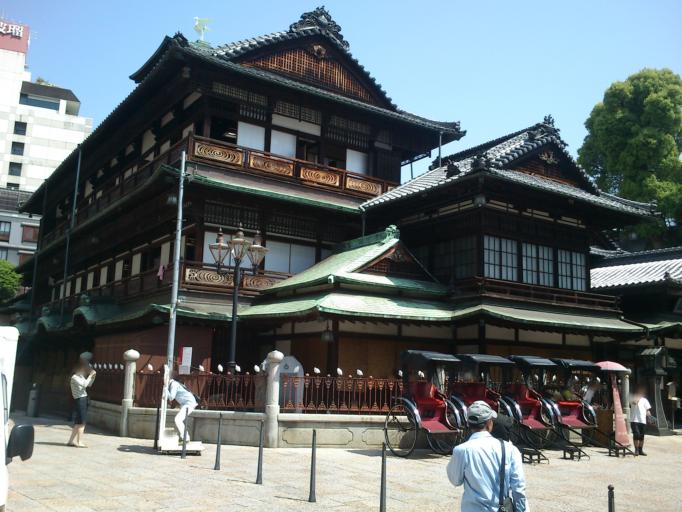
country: JP
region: Ehime
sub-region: Shikoku-chuo Shi
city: Matsuyama
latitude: 33.8498
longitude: 132.7866
